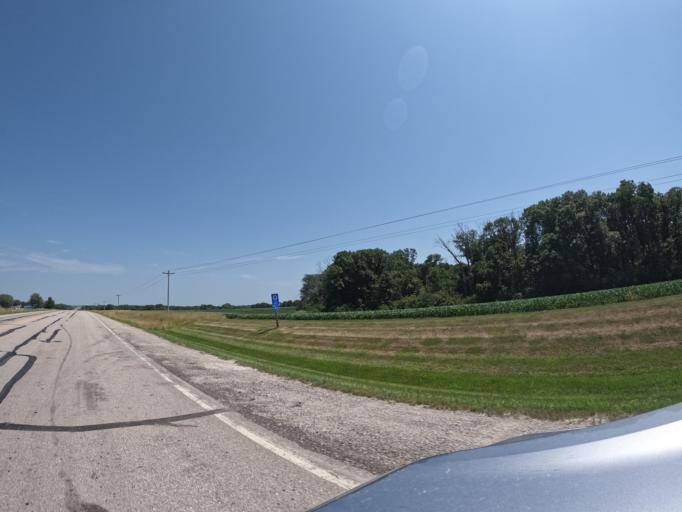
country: US
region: Iowa
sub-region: Henry County
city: Mount Pleasant
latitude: 40.9671
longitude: -91.6216
